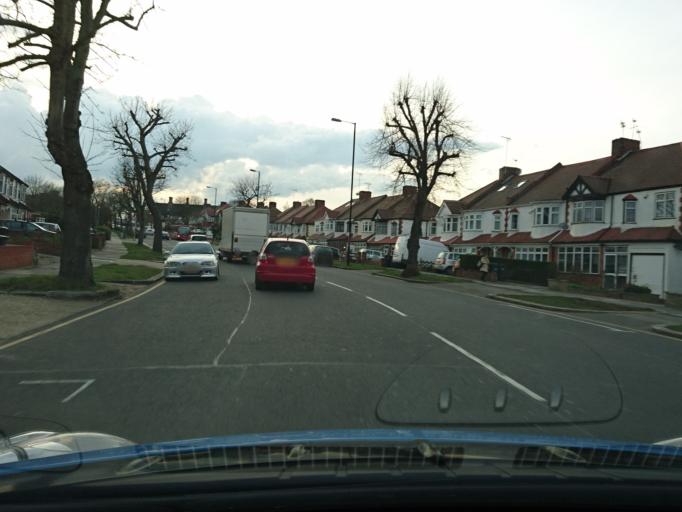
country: GB
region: England
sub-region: Greater London
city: Wood Green
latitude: 51.6154
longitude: -0.1288
